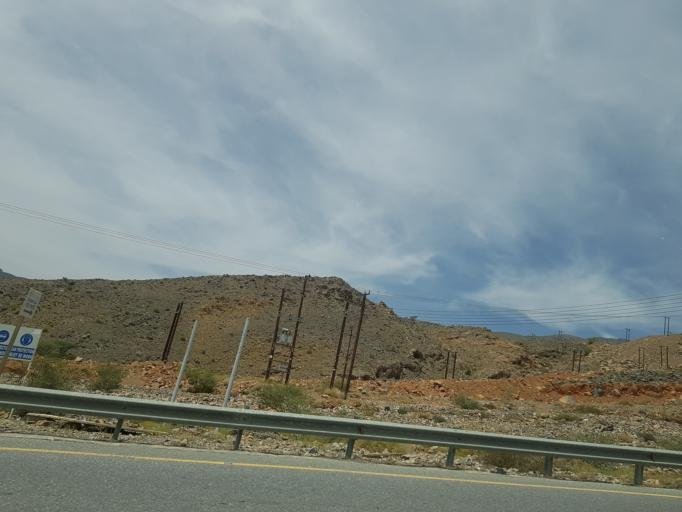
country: OM
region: Muhafazat ad Dakhiliyah
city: Izki
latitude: 22.9789
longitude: 57.7005
